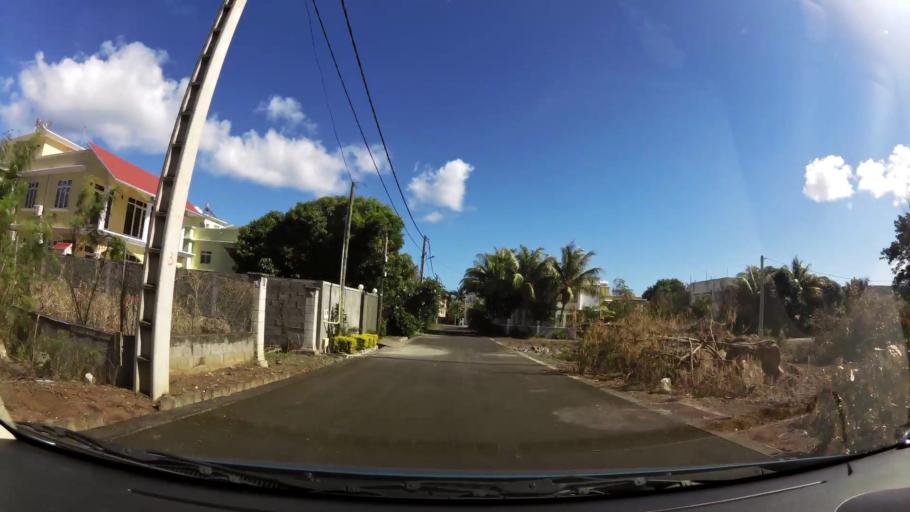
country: MU
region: Black River
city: Flic en Flac
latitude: -20.2850
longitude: 57.3721
